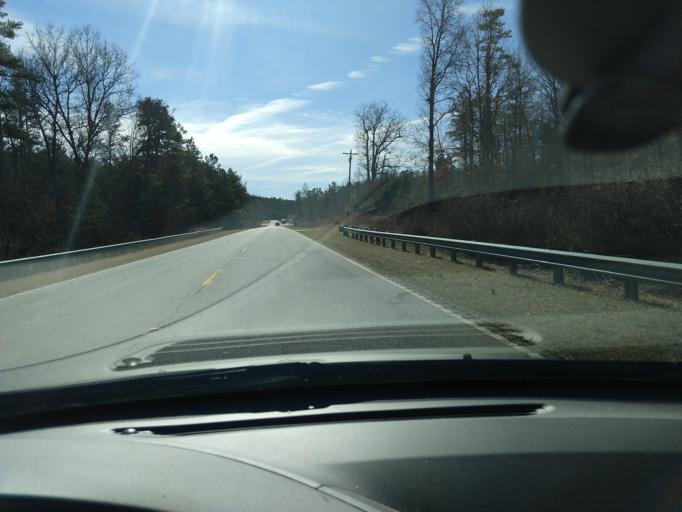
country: US
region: South Carolina
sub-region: Oconee County
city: Westminster
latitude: 34.6274
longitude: -83.1363
